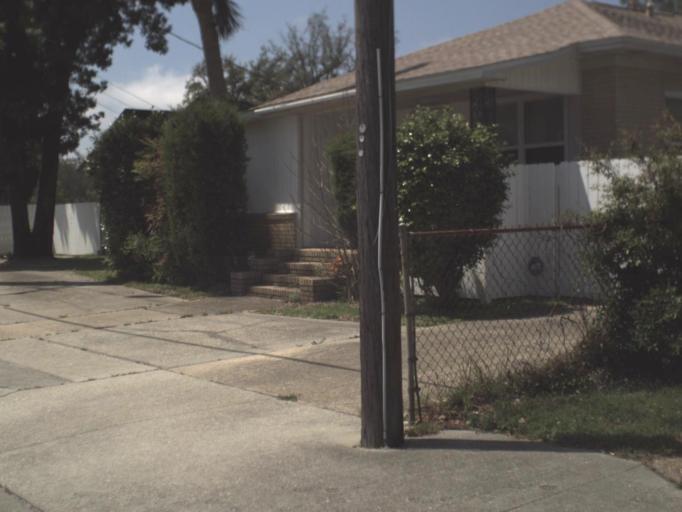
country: US
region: Florida
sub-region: Escambia County
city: Warrington
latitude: 30.3803
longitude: -87.2773
